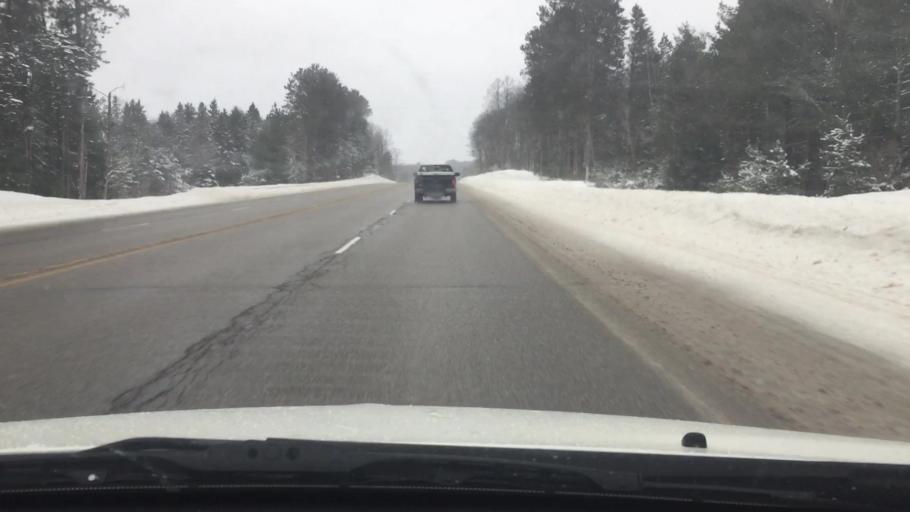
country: US
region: Michigan
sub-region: Otsego County
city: Gaylord
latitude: 45.0460
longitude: -84.7758
